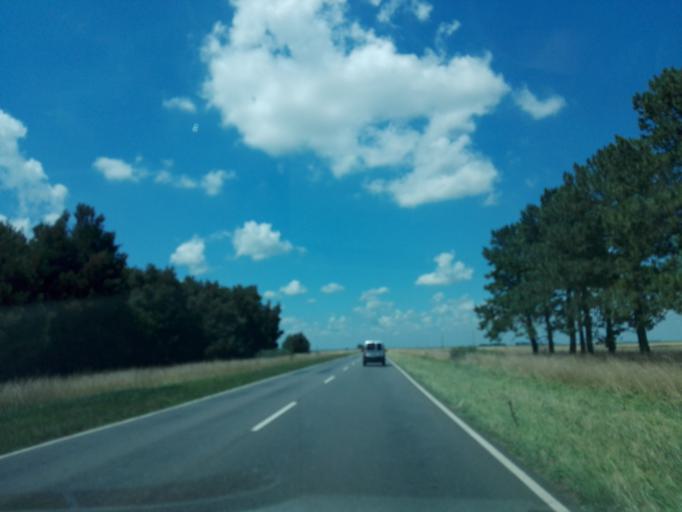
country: AR
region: Buenos Aires
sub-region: Partido de General Belgrano
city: General Belgrano
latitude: -35.9164
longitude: -58.6195
